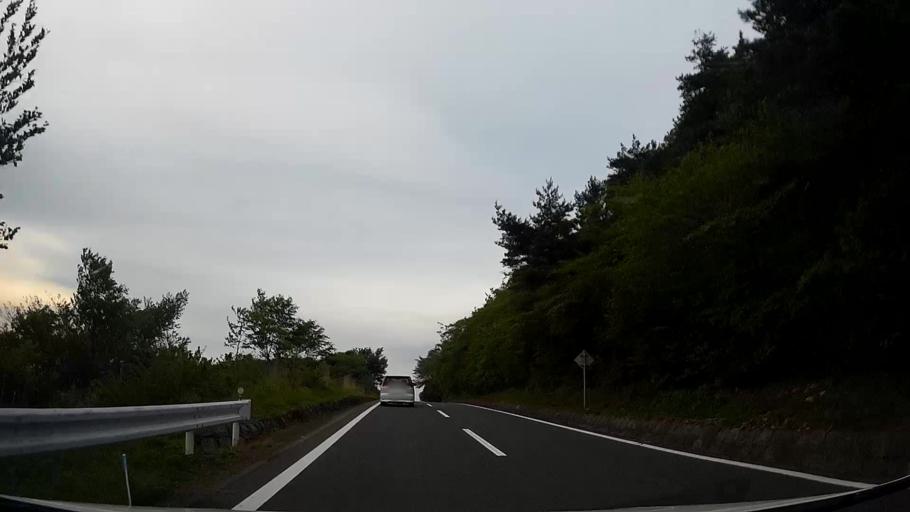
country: JP
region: Shizuoka
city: Atami
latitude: 35.0750
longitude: 139.0271
